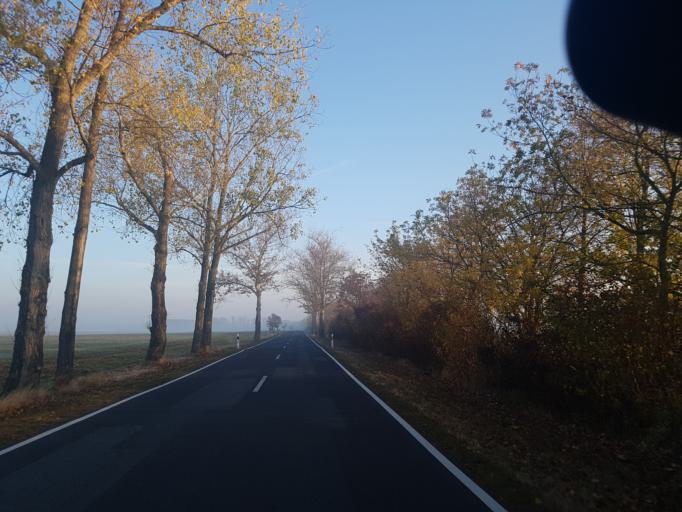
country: DE
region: Brandenburg
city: Juterbog
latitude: 51.9202
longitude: 13.0868
